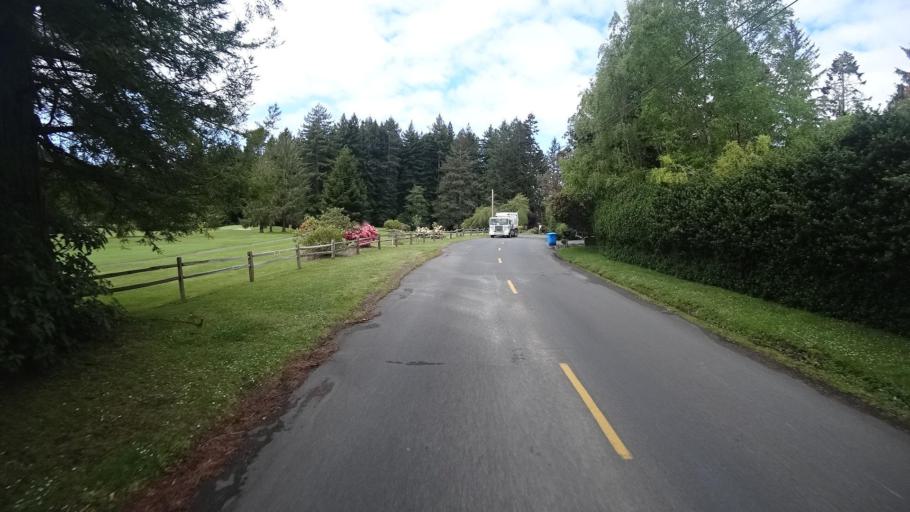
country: US
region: California
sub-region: Humboldt County
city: Bayside
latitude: 40.8527
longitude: -124.0554
